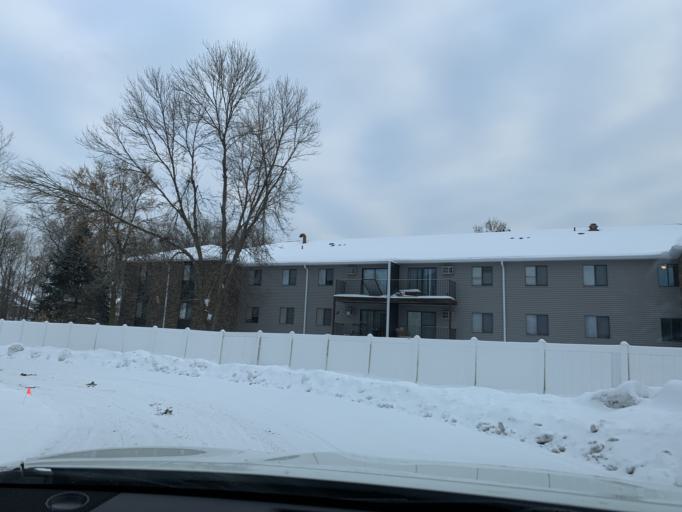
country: US
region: Minnesota
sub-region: Anoka County
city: Coon Rapids
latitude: 45.1644
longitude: -93.2927
